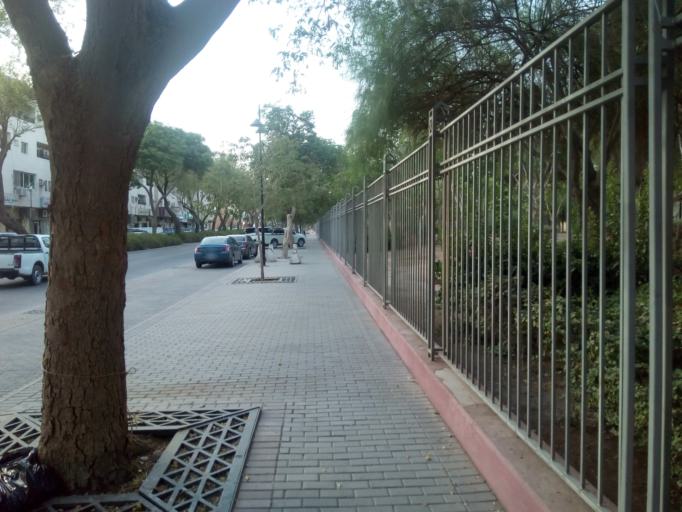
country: SA
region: Ar Riyad
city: Riyadh
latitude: 24.6453
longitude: 46.7078
